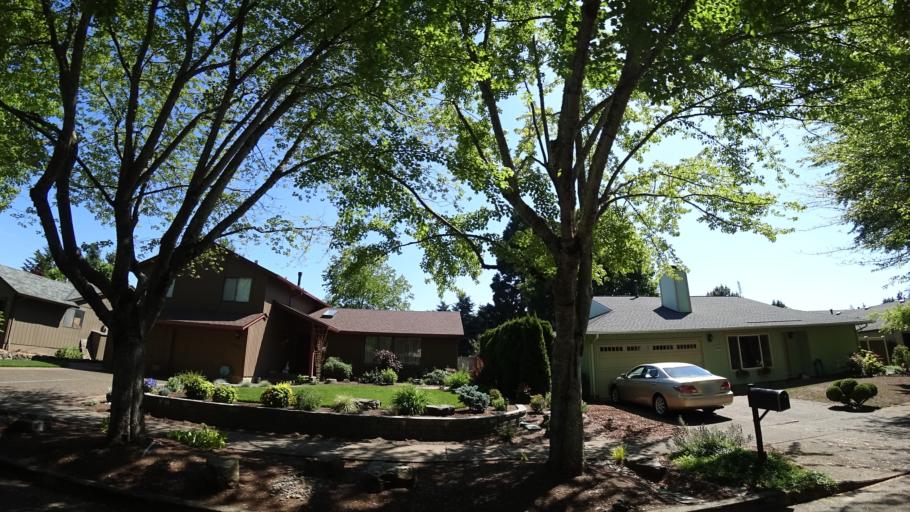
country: US
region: Oregon
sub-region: Washington County
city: Beaverton
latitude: 45.4469
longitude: -122.8134
